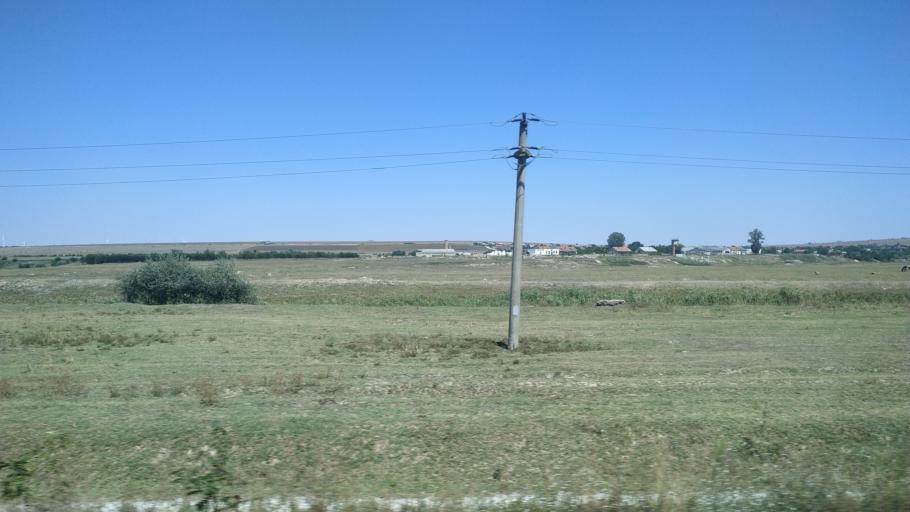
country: RO
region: Constanta
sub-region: Comuna Mircea Voda
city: Satu Nou
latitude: 44.2598
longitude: 28.2132
